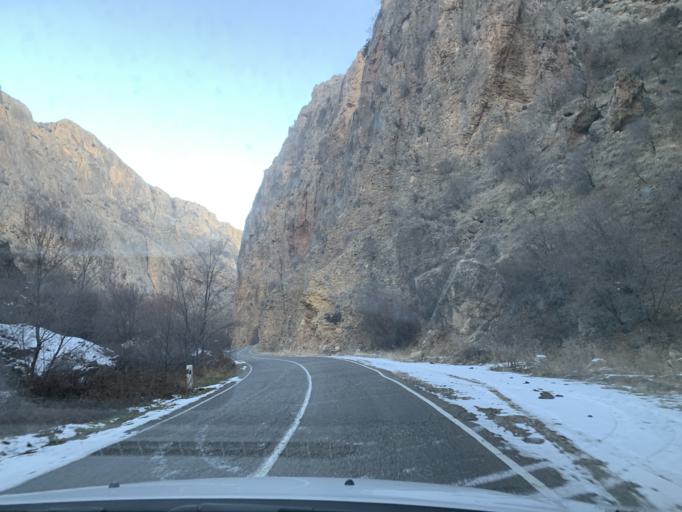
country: AM
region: Vayots' Dzori Marz
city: Areni
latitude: 39.7165
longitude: 45.2064
